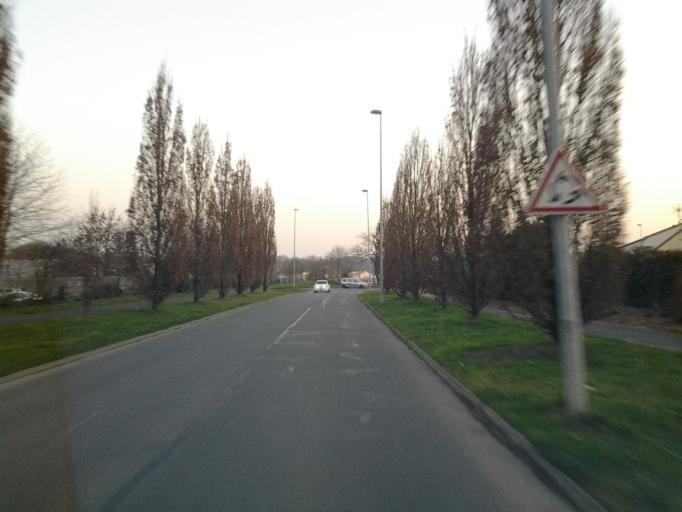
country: FR
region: Pays de la Loire
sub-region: Departement de la Vendee
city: La Roche-sur-Yon
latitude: 46.6555
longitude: -1.4105
